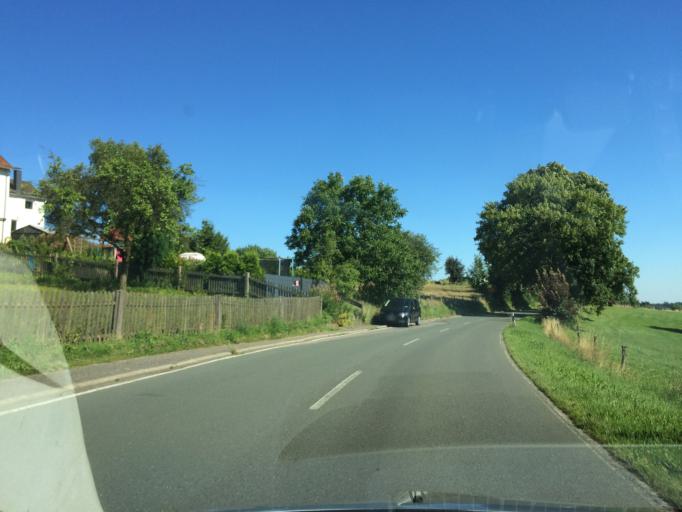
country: DE
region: North Rhine-Westphalia
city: Iserlohn
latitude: 51.3373
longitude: 7.7067
